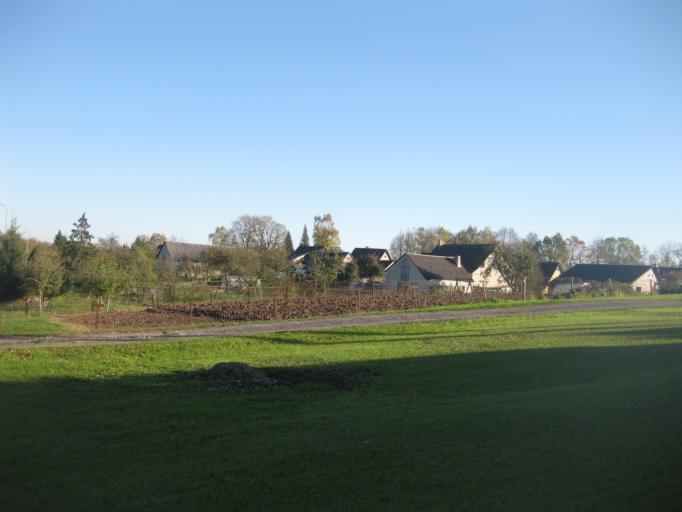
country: LT
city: Vilkija
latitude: 55.0413
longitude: 23.5932
